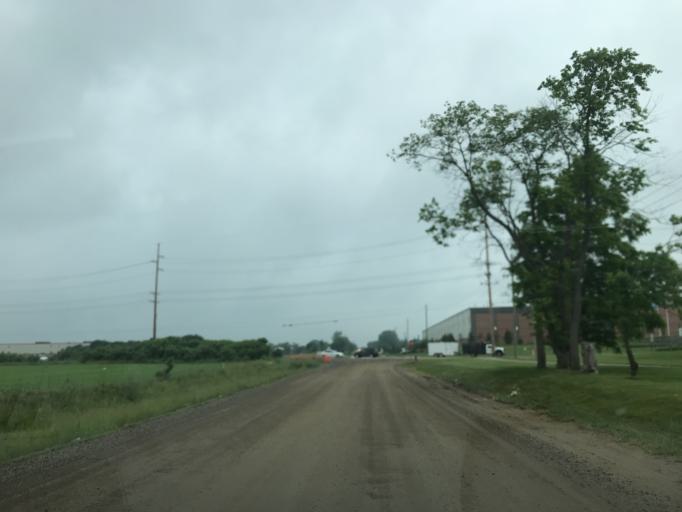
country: US
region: Michigan
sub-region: Oakland County
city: Wixom
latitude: 42.5063
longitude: -83.5957
